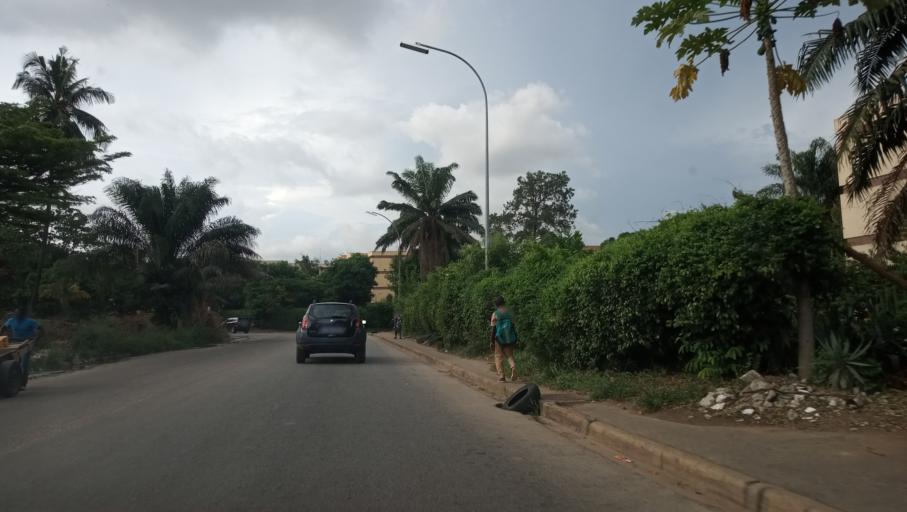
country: CI
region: Lagunes
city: Abidjan
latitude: 5.3429
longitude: -3.9760
